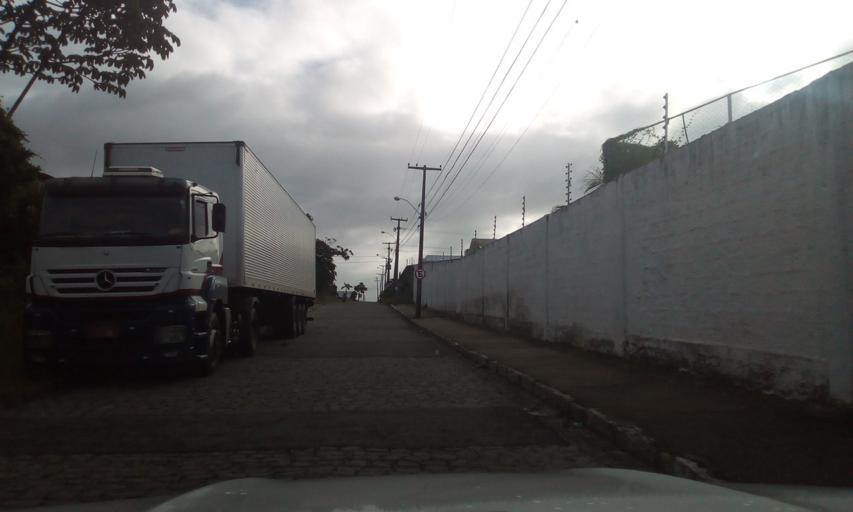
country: BR
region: Paraiba
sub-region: Joao Pessoa
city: Joao Pessoa
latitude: -7.1570
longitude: -34.8168
